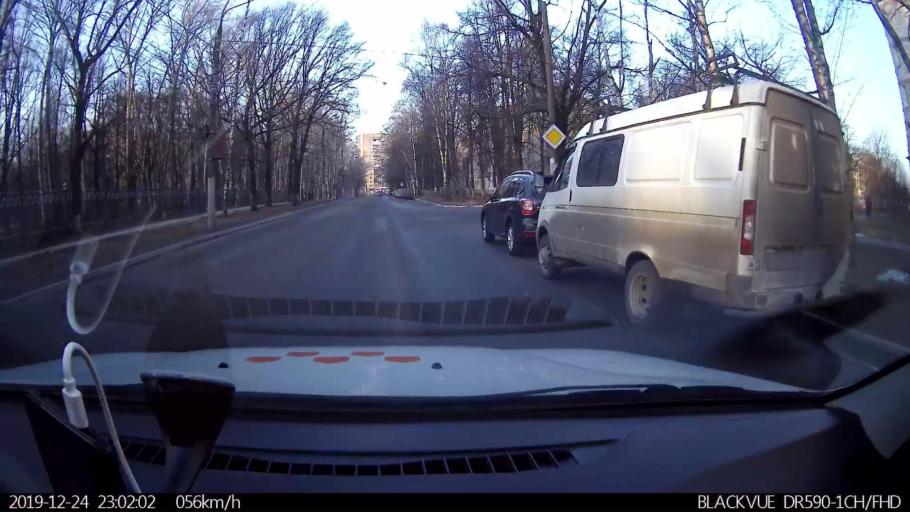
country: RU
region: Nizjnij Novgorod
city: Nizhniy Novgorod
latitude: 56.2698
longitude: 43.9217
